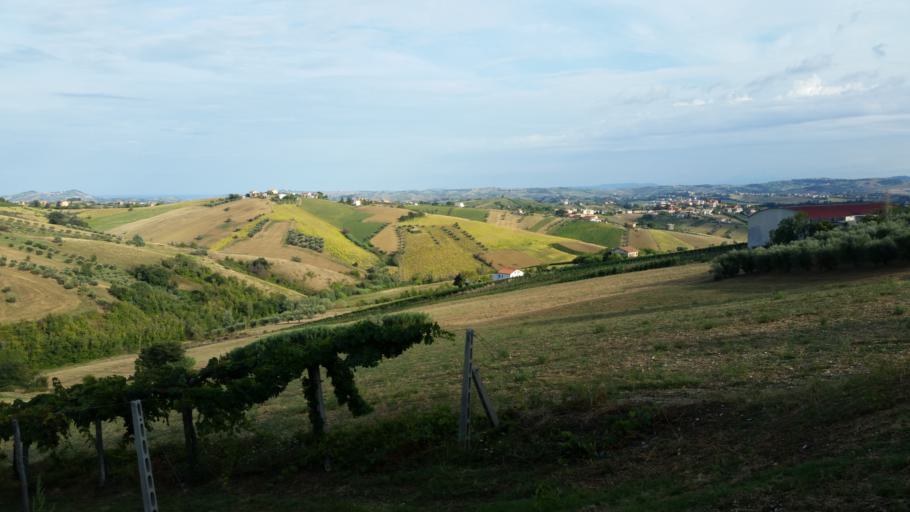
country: IT
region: Abruzzo
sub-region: Provincia di Teramo
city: Torano Nuovo
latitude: 42.8396
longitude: 13.7665
